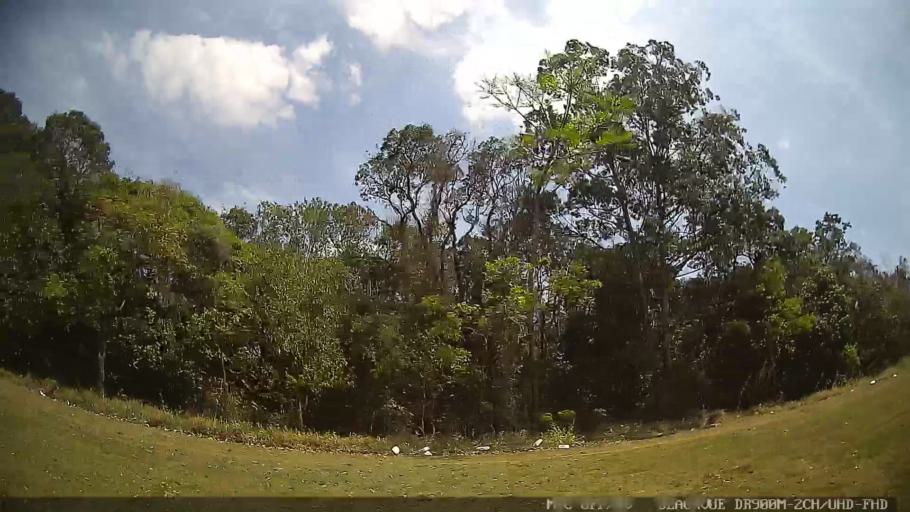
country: BR
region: Sao Paulo
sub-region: Itupeva
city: Itupeva
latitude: -23.2498
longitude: -47.0474
